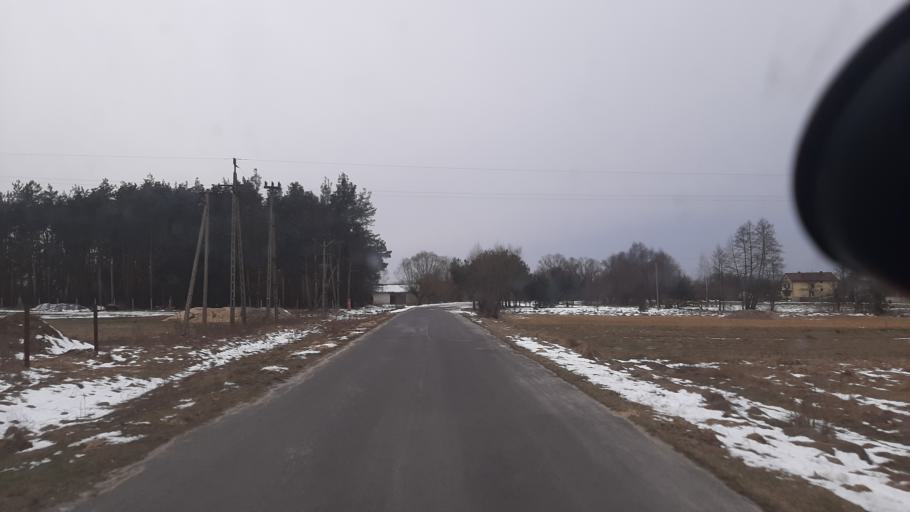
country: PL
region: Lublin Voivodeship
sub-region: Powiat lubartowski
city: Kamionka
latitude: 51.5166
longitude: 22.4796
